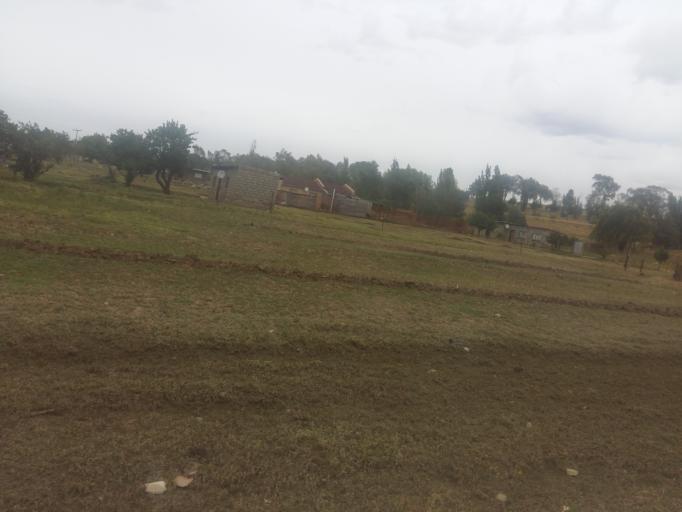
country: LS
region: Mafeteng
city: Mafeteng
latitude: -29.6957
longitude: 27.4372
